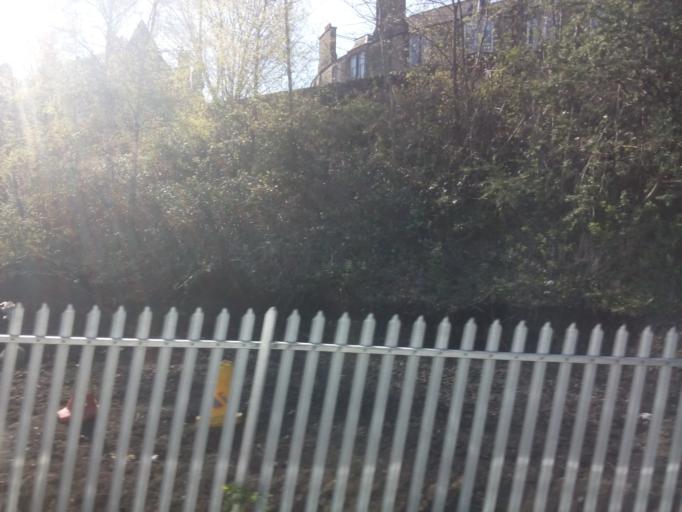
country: GB
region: Scotland
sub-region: West Lothian
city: Seafield
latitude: 55.9557
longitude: -3.1543
